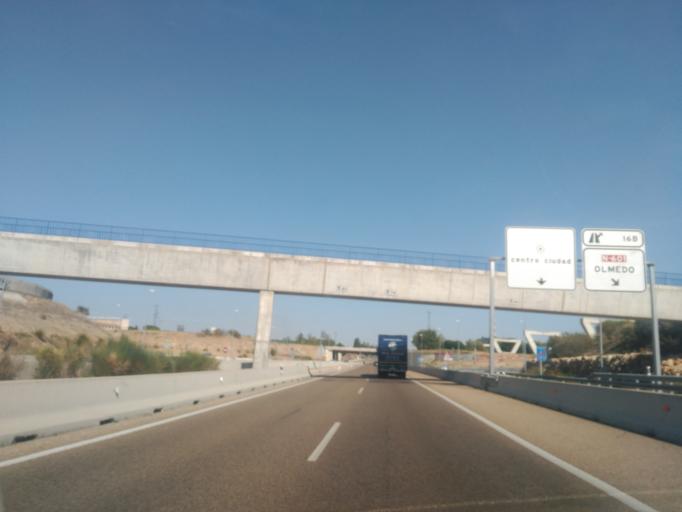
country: ES
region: Castille and Leon
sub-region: Provincia de Valladolid
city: Laguna de Duero
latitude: 41.6080
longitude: -4.7292
